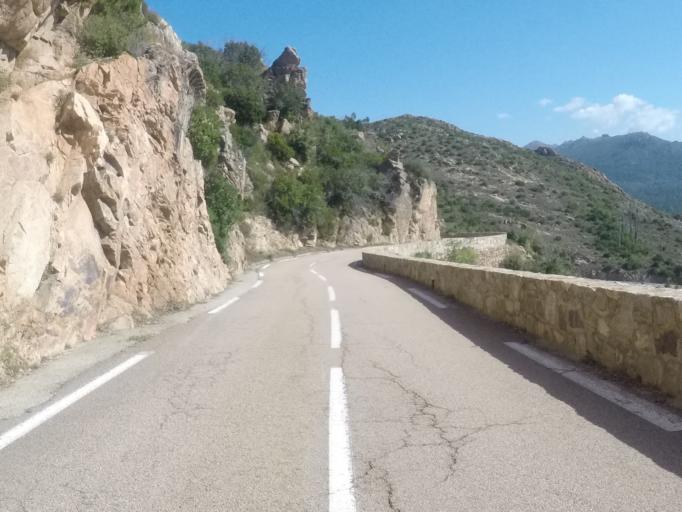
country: FR
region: Corsica
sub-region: Departement de la Corse-du-Sud
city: Zonza
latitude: 41.7675
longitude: 9.0518
